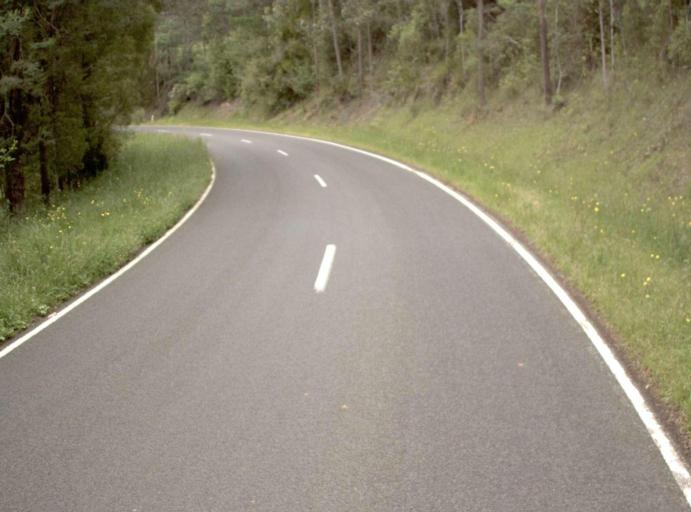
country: AU
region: Victoria
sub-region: Baw Baw
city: Warragul
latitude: -37.8873
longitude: 146.0891
